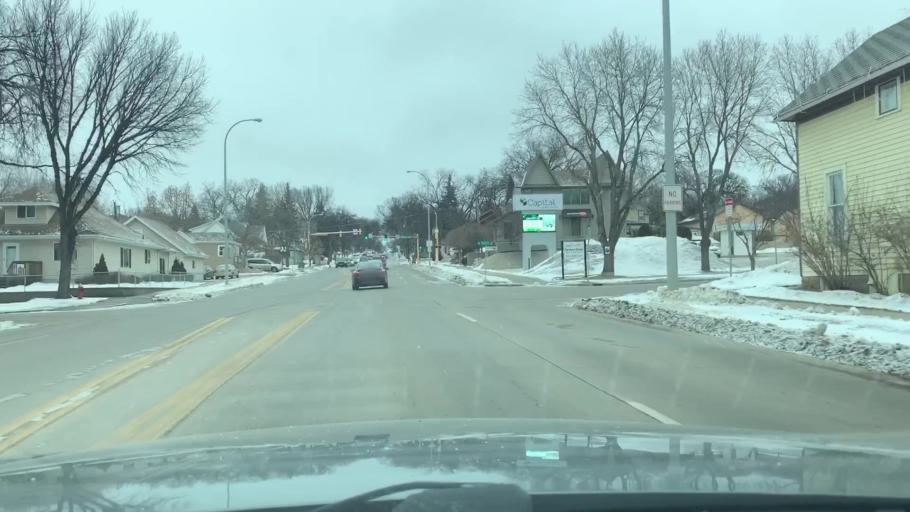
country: US
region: North Dakota
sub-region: Burleigh County
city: Bismarck
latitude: 46.8074
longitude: -100.7943
